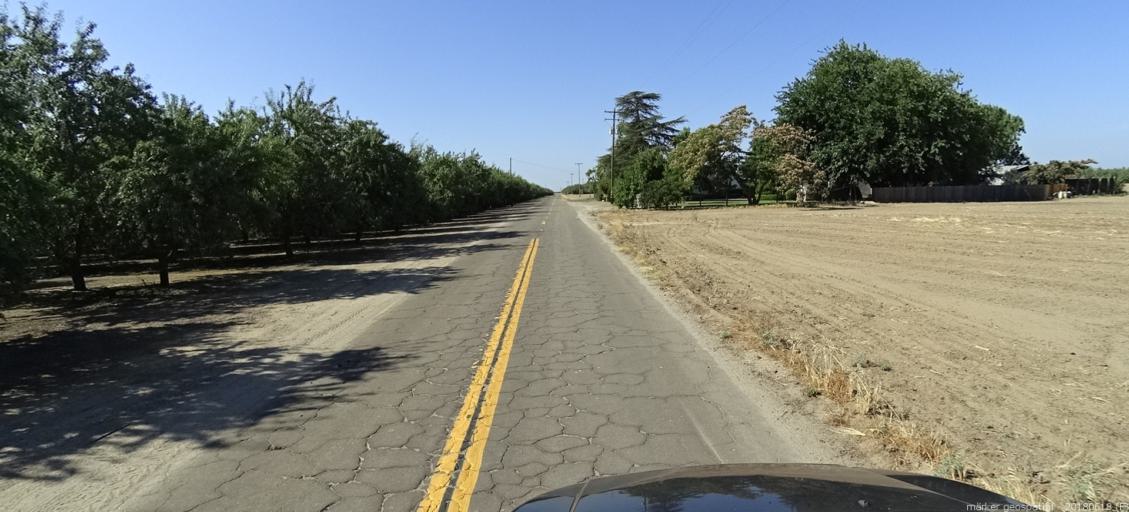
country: US
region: California
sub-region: Madera County
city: Madera
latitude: 36.9053
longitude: -120.1377
